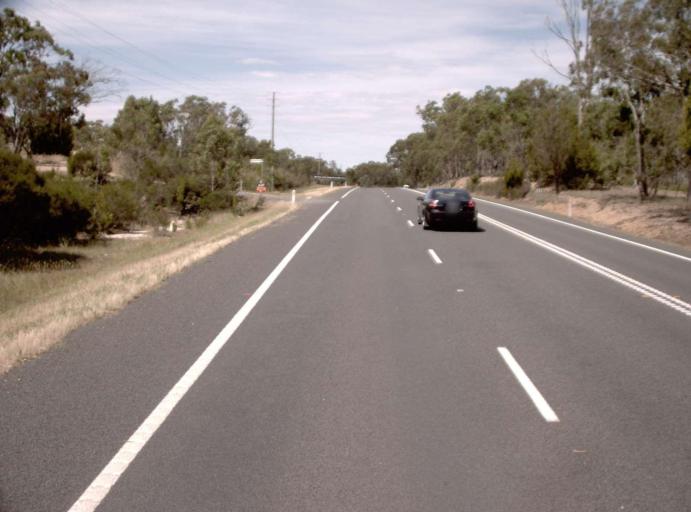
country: AU
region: Victoria
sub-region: Wellington
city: Sale
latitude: -37.9455
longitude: 147.1237
